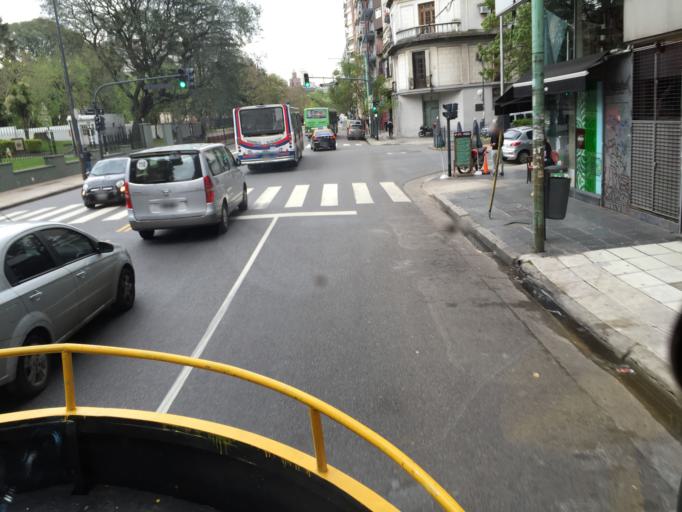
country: AR
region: Buenos Aires F.D.
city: Colegiales
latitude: -34.5730
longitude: -58.4331
